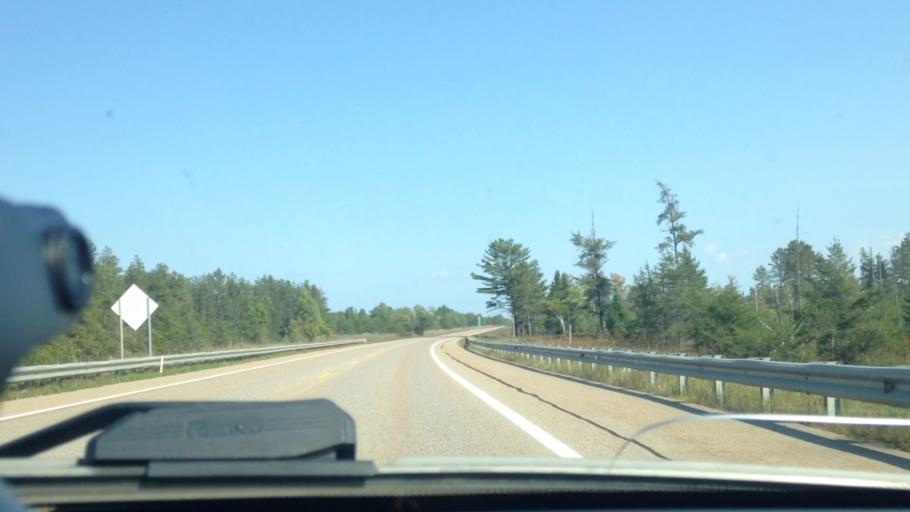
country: US
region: Michigan
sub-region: Mackinac County
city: Saint Ignace
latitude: 46.3581
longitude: -84.8864
